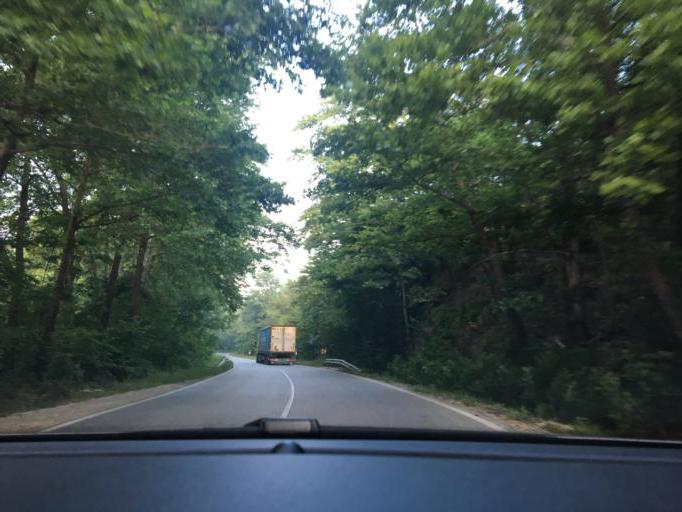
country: BG
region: Blagoevgrad
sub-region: Obshtina Petrich
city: Petrich
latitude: 41.4002
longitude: 23.0770
